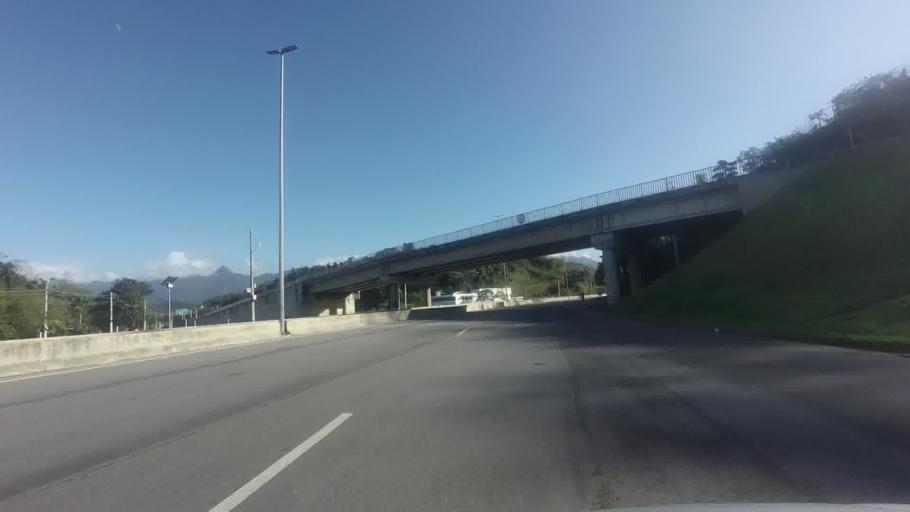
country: BR
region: Rio de Janeiro
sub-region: Petropolis
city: Petropolis
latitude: -22.6082
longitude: -43.2860
